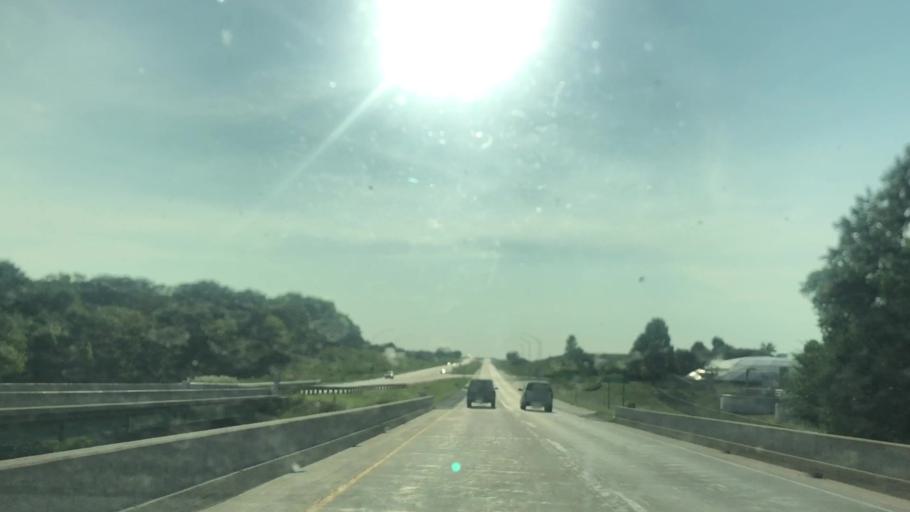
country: US
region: Iowa
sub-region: Story County
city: Nevada
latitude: 42.0055
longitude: -93.4501
